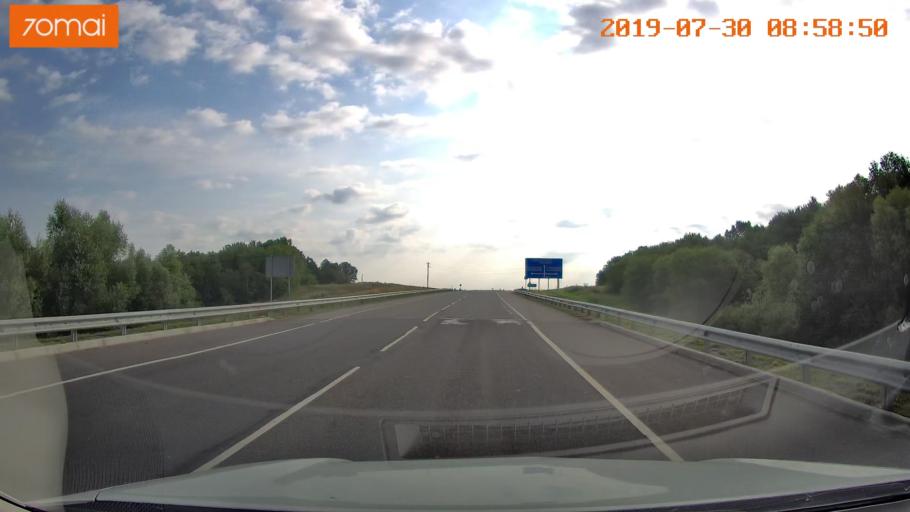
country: RU
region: Kaliningrad
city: Gusev
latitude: 54.6120
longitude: 22.1391
